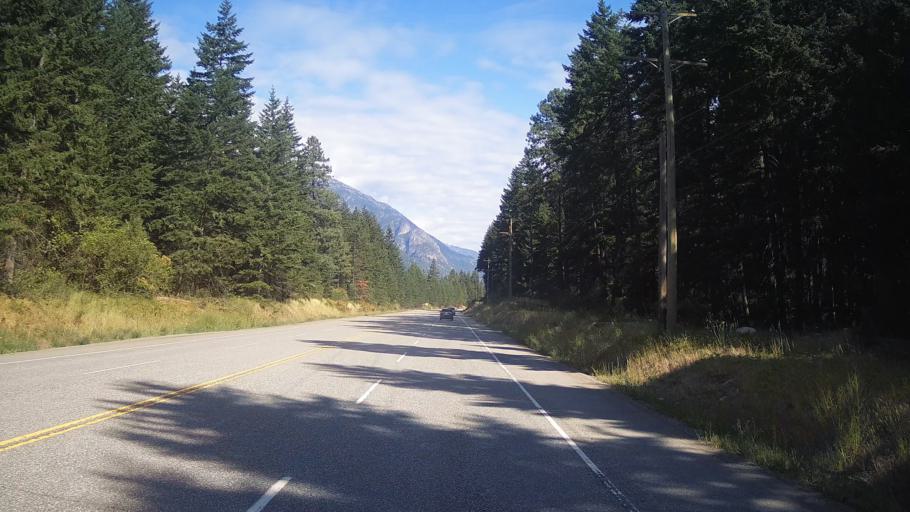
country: CA
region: British Columbia
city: Hope
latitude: 50.0462
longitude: -121.5388
